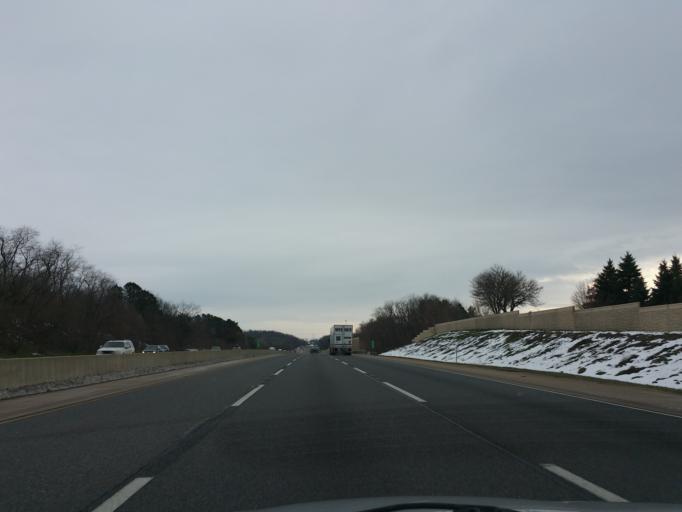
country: US
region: Illinois
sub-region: Winnebago County
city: Roscoe
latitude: 42.4042
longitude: -88.9832
